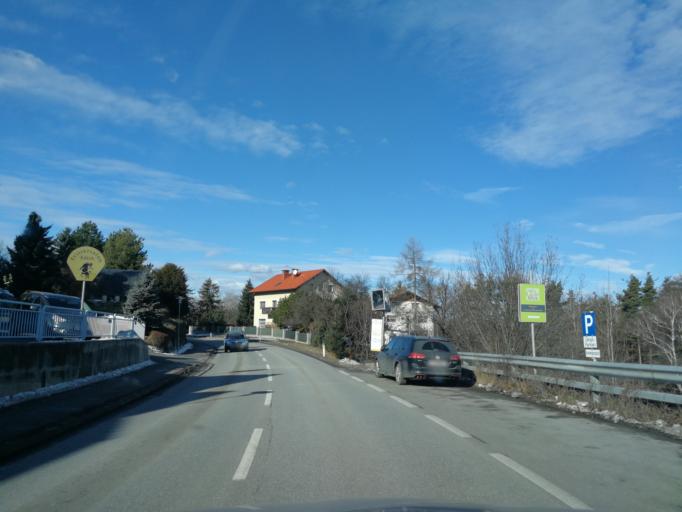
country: AT
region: Styria
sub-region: Politischer Bezirk Graz-Umgebung
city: Nestelbach bei Graz
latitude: 47.0565
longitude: 15.6038
